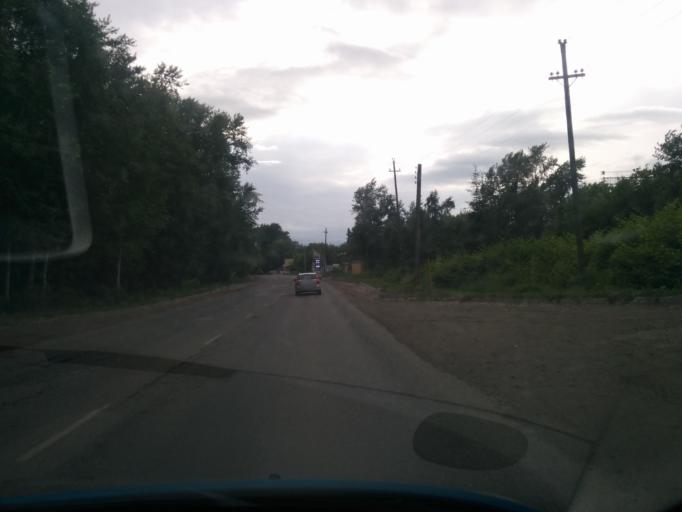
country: RU
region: Perm
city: Perm
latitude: 58.0032
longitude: 56.1866
